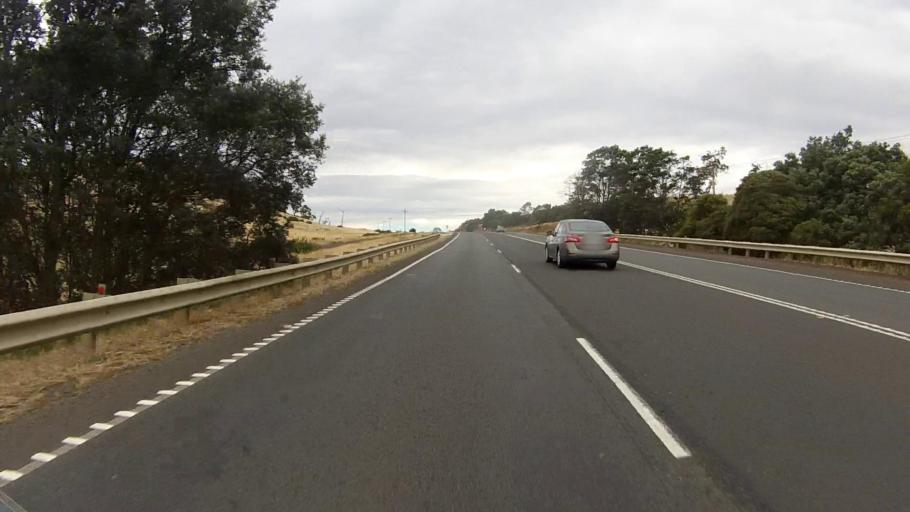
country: AU
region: Tasmania
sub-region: Brighton
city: Bridgewater
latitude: -42.3397
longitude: 147.3412
